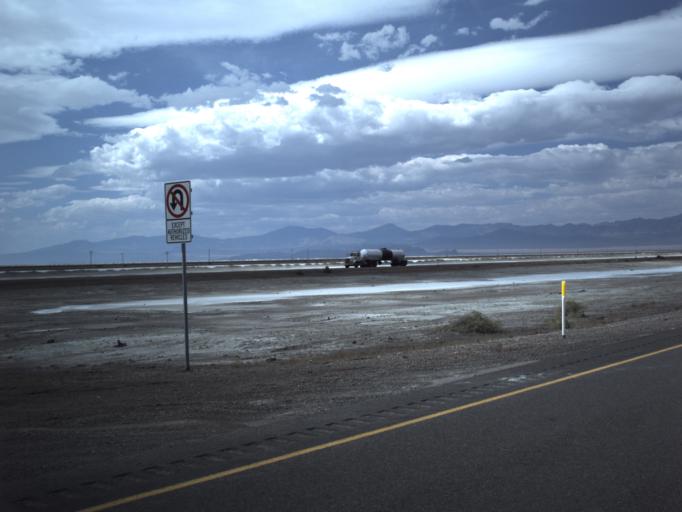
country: US
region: Utah
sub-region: Tooele County
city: Wendover
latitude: 40.7406
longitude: -113.9112
